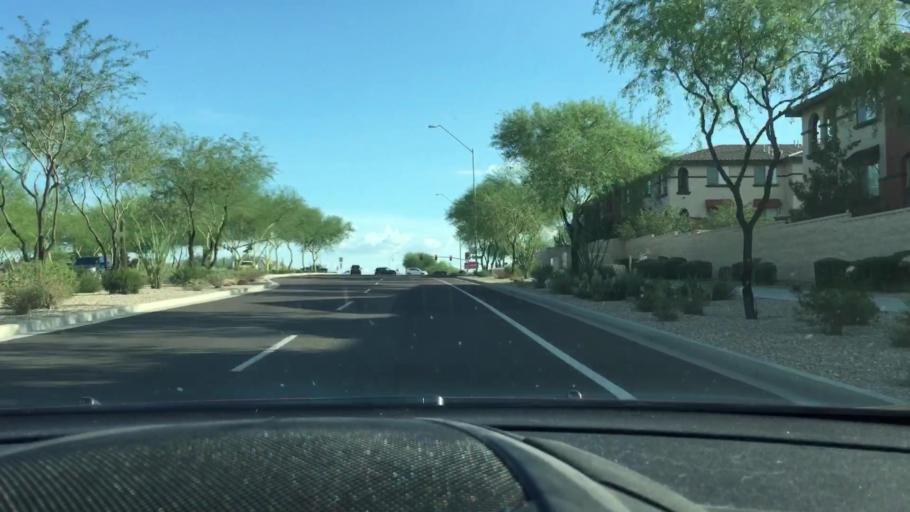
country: US
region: Arizona
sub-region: Maricopa County
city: Sun City West
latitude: 33.7155
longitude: -112.2853
